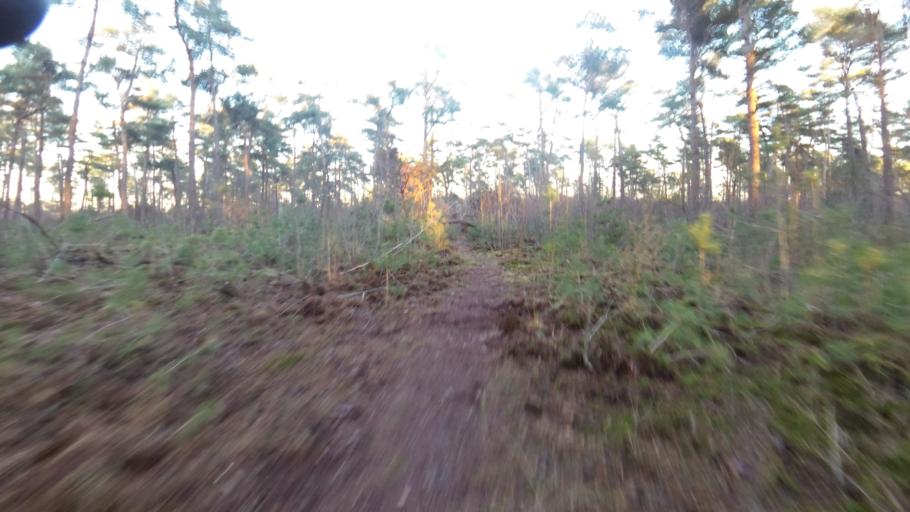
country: NL
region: Gelderland
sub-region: Gemeente Apeldoorn
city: Uddel
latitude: 52.2036
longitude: 5.7689
